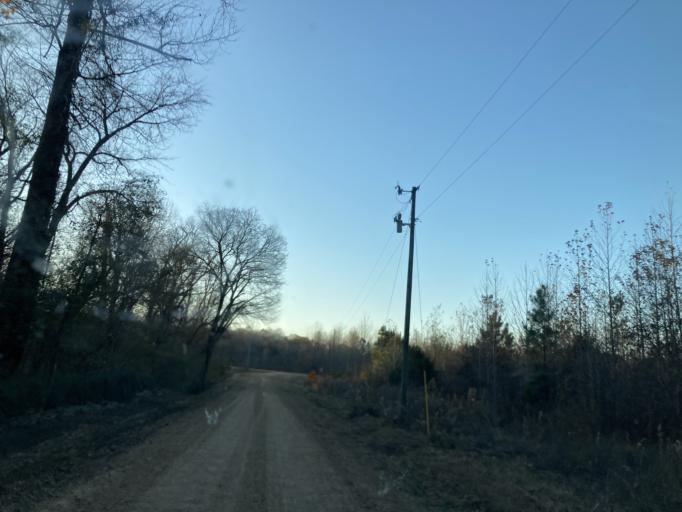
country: US
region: Mississippi
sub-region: Yazoo County
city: Yazoo City
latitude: 32.9719
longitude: -90.2634
